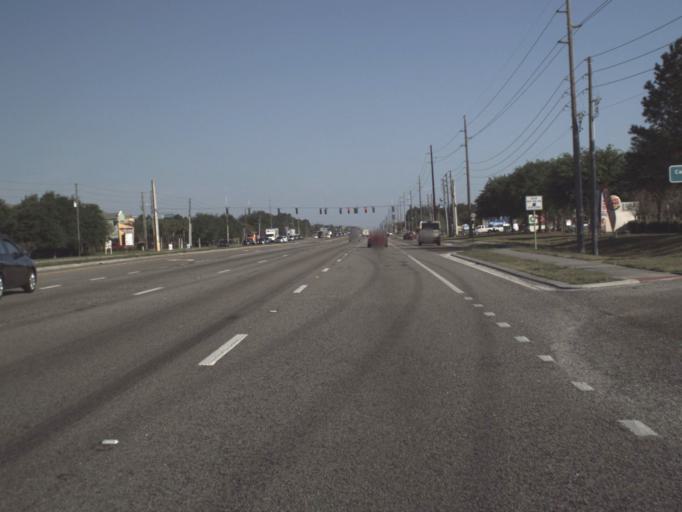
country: US
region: Florida
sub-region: Lake County
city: Four Corners
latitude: 28.3533
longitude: -81.6761
